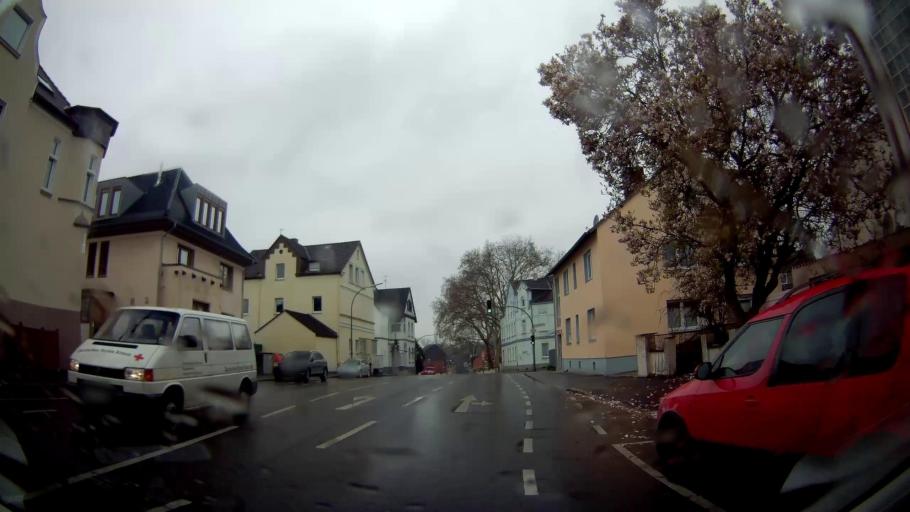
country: DE
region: North Rhine-Westphalia
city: Witten
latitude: 51.5021
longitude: 7.3387
